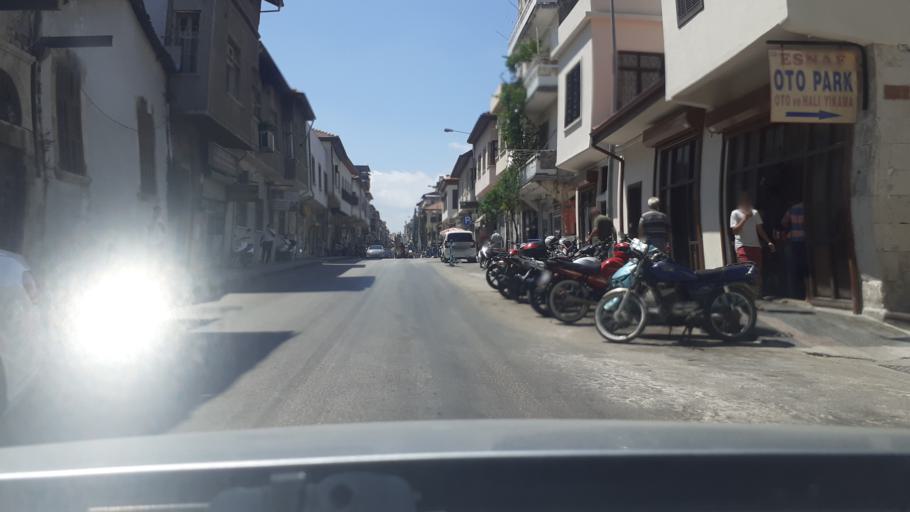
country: TR
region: Hatay
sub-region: Antakya Ilcesi
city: Antakya
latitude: 36.2005
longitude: 36.1647
